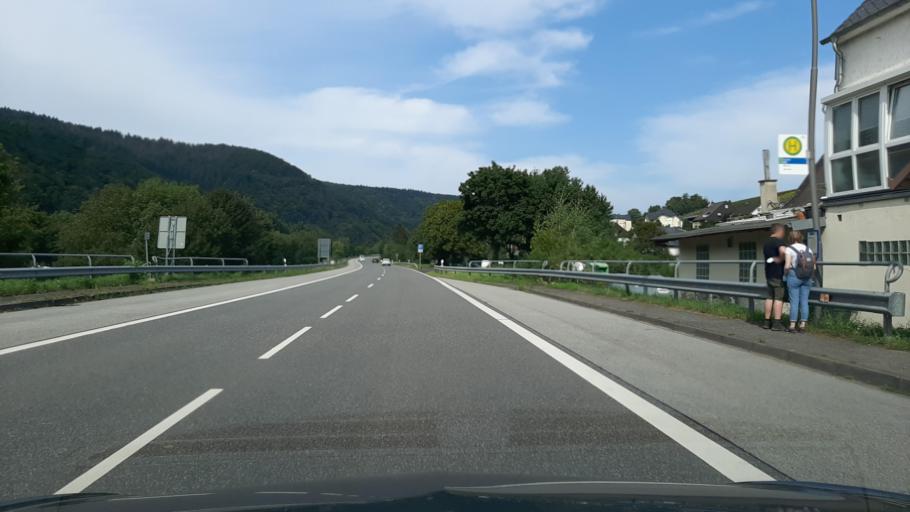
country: DE
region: Rheinland-Pfalz
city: Enkirch
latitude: 49.9847
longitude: 7.1217
